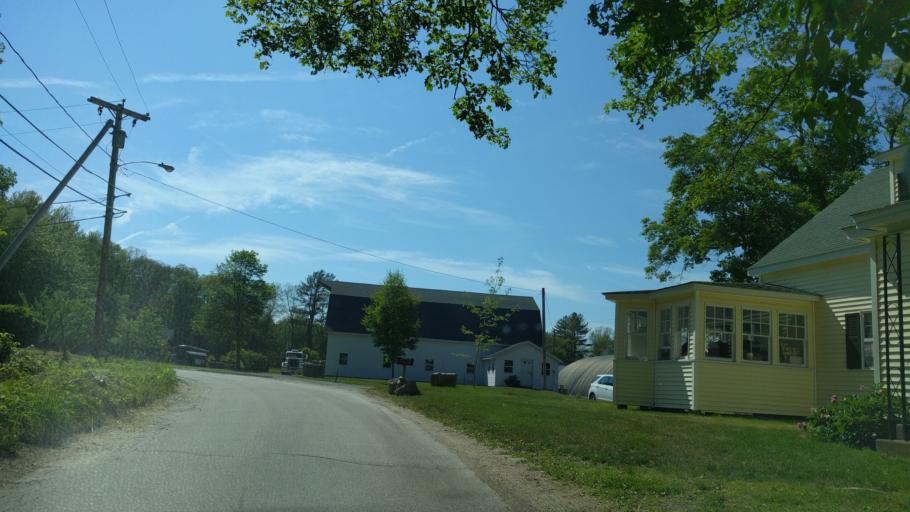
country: US
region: Massachusetts
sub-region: Worcester County
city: East Douglas
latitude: 42.0803
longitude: -71.7322
